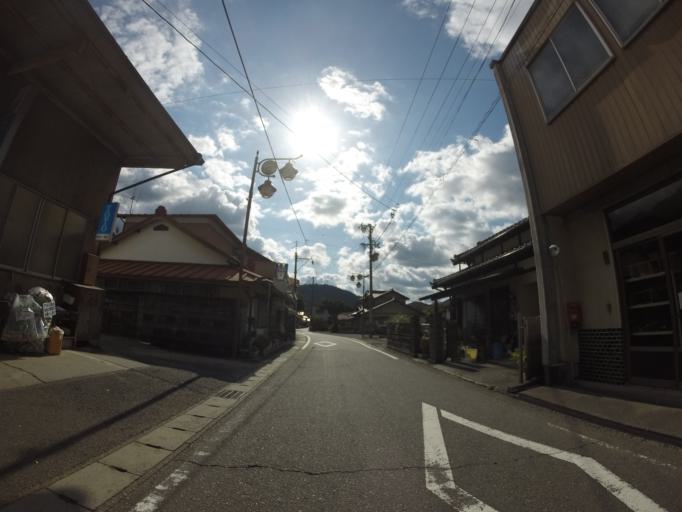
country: JP
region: Shizuoka
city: Fujieda
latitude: 35.1084
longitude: 138.1417
